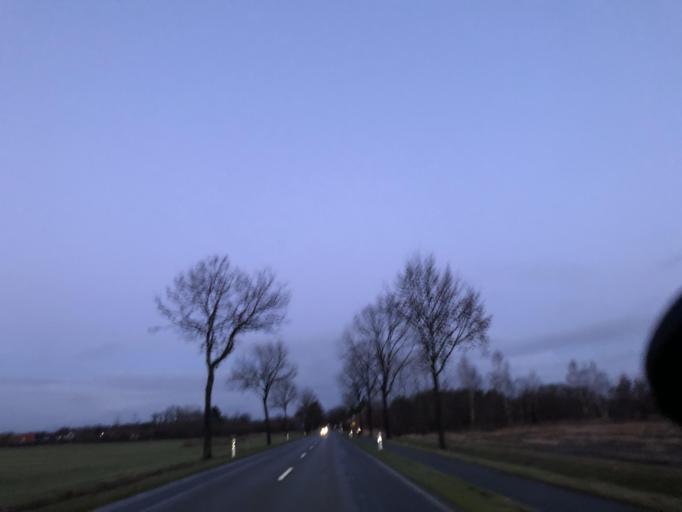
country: DE
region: Lower Saxony
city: Wietzendorf
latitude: 52.9189
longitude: 9.9604
